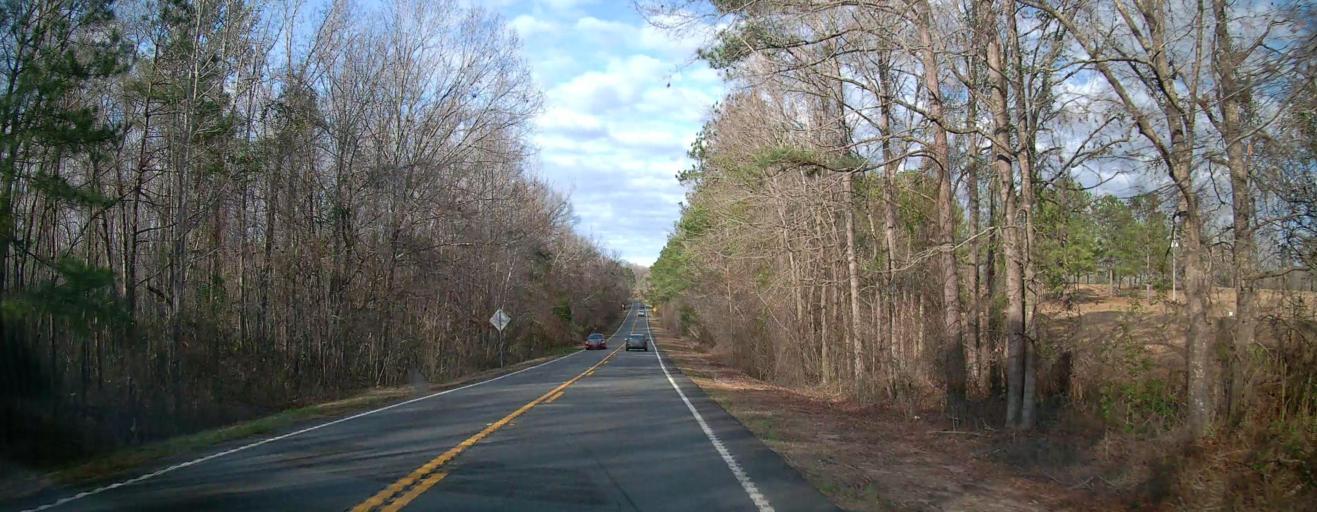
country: US
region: Georgia
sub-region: Talbot County
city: Talbotton
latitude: 32.5393
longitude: -84.6029
